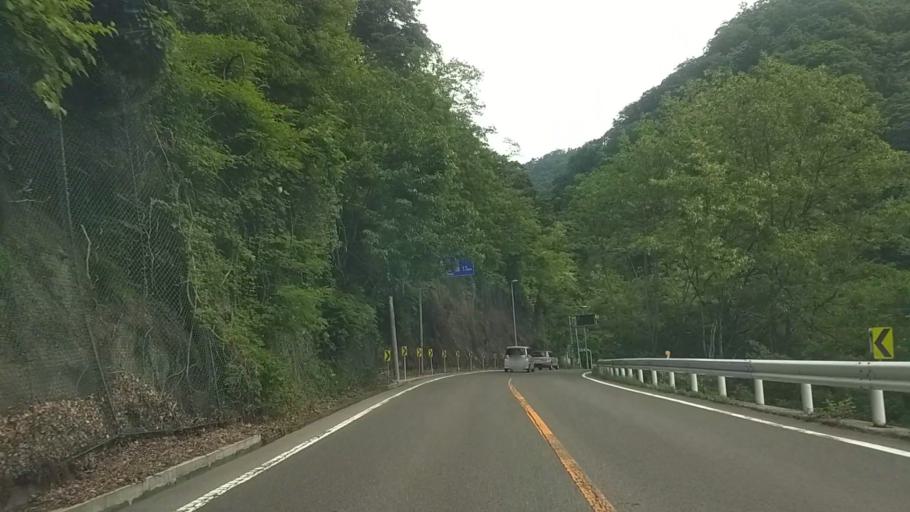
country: JP
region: Yamanashi
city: Isawa
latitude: 35.5580
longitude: 138.5902
